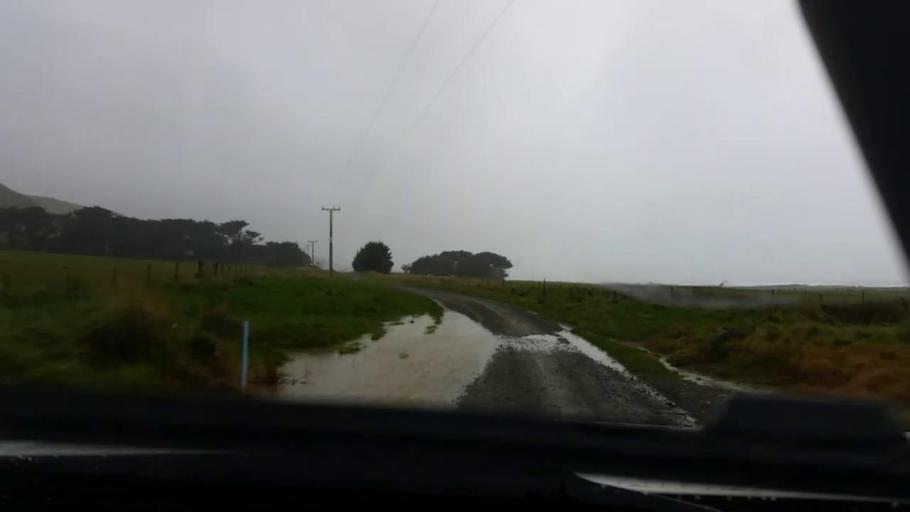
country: NZ
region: Wellington
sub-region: Masterton District
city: Masterton
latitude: -41.2594
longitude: 175.8991
